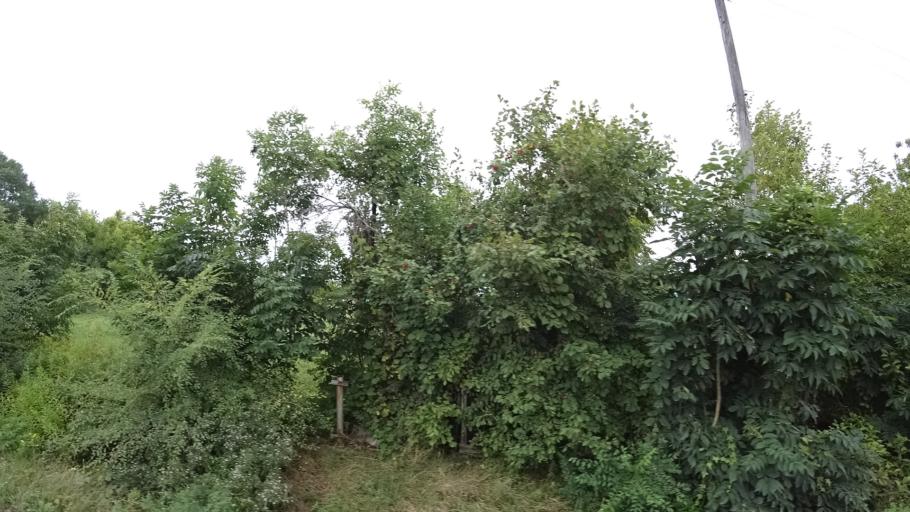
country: RU
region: Primorskiy
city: Chernigovka
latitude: 44.3376
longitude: 132.5695
